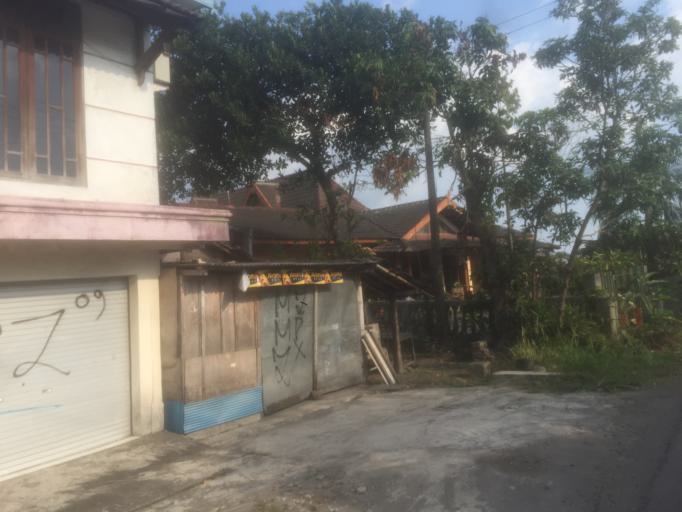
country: ID
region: Daerah Istimewa Yogyakarta
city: Sleman
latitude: -7.6468
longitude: 110.4243
